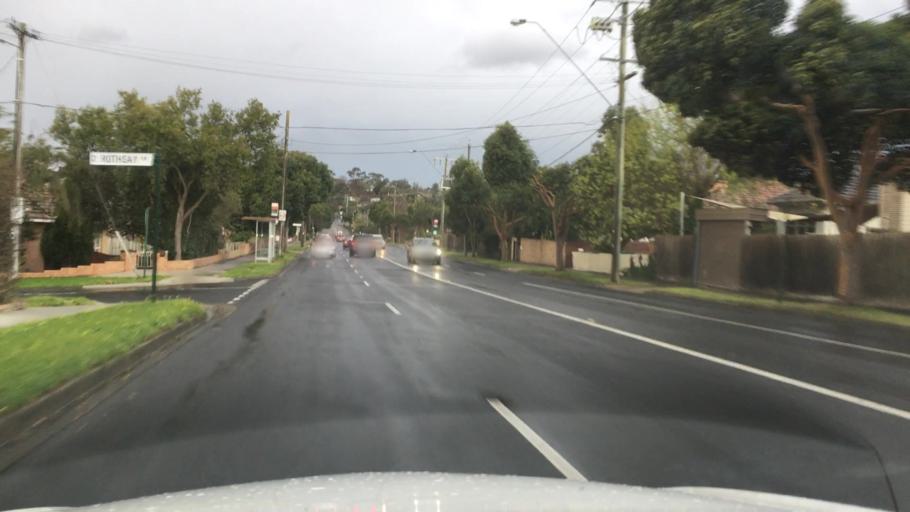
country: AU
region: Victoria
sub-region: Whitehorse
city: Burwood
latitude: -37.8442
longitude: 145.1211
